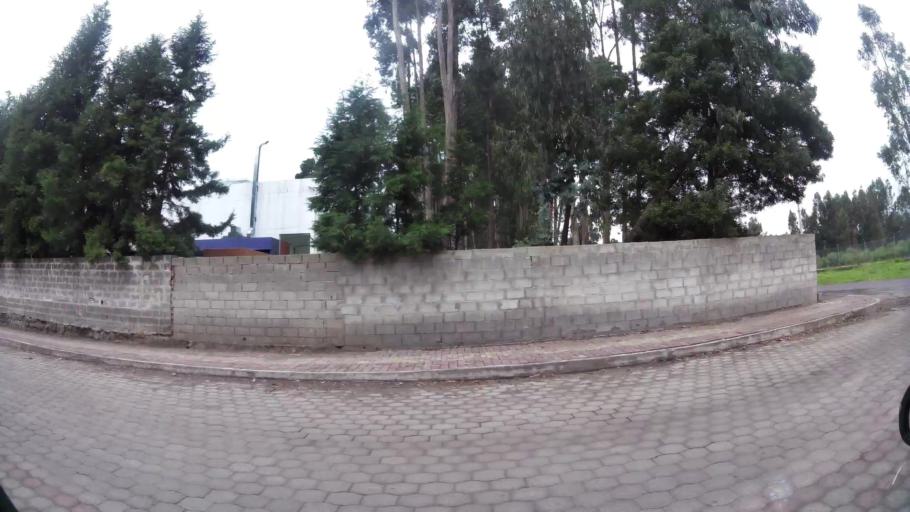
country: EC
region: Pichincha
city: Sangolqui
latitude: -0.3462
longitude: -78.4702
